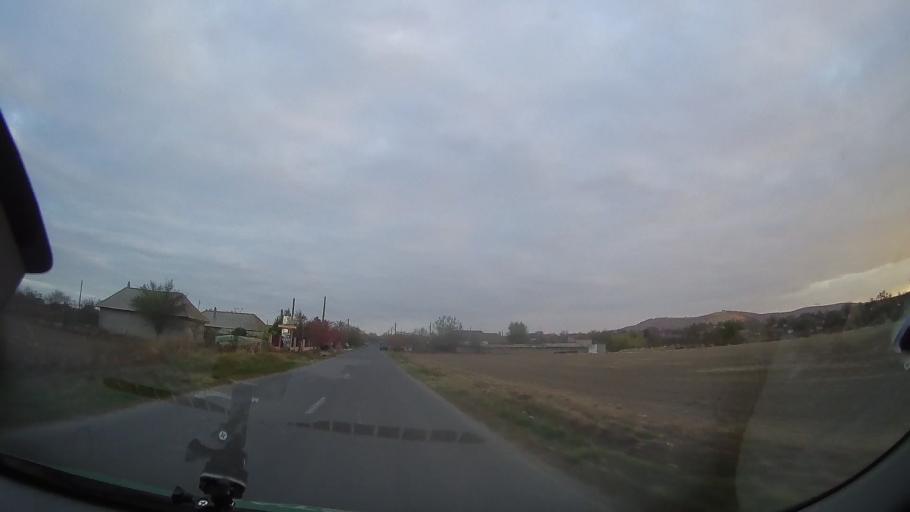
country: RO
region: Tulcea
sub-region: Comuna Mihai Bravu
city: Turda
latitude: 44.9818
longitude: 28.6149
